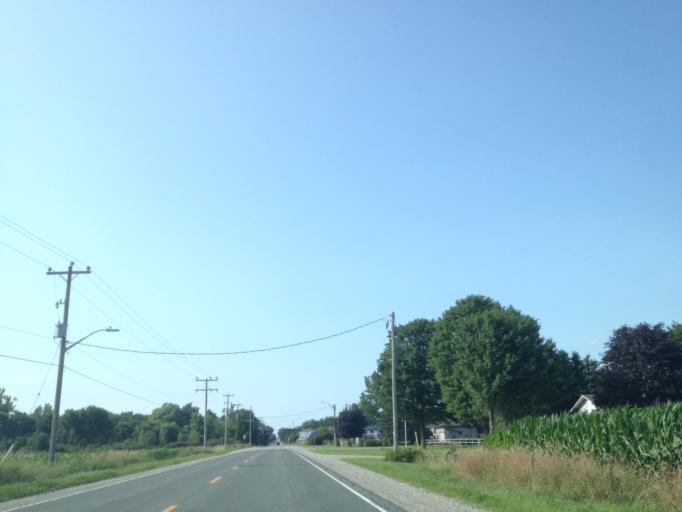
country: CA
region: Ontario
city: Aylmer
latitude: 42.8510
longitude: -80.8367
